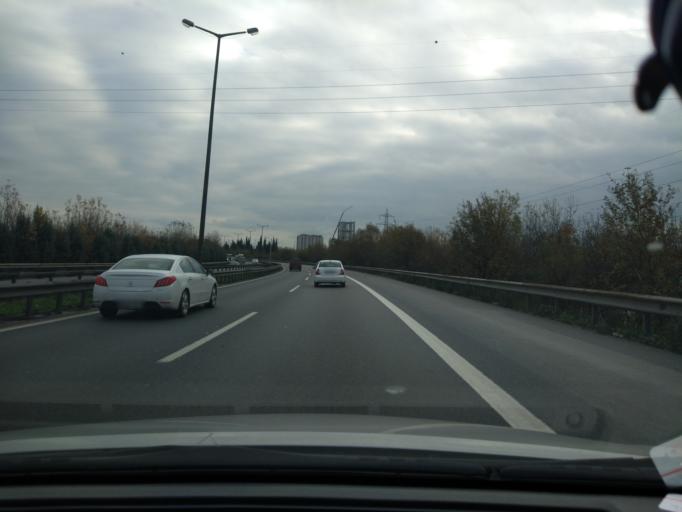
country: TR
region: Kocaeli
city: Kosekoy
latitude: 40.7706
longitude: 29.9864
